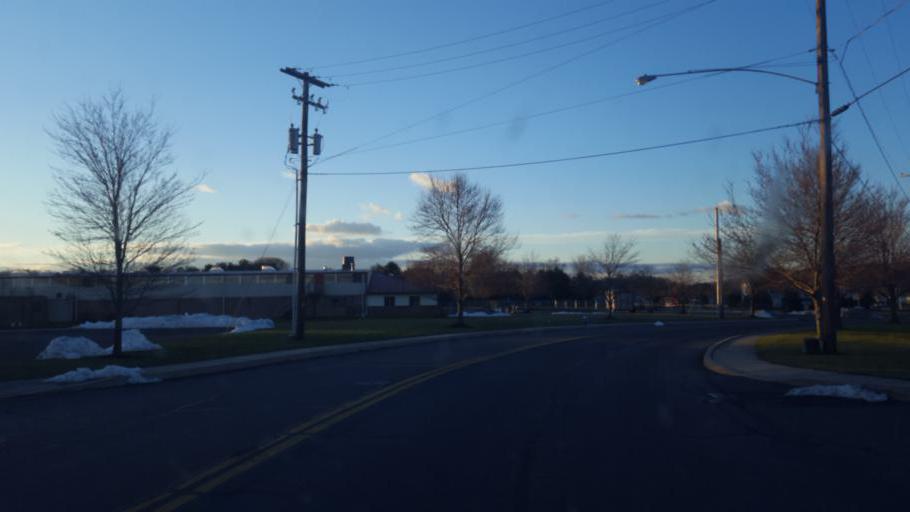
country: US
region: Pennsylvania
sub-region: Lancaster County
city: New Holland
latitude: 40.0899
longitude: -76.0878
